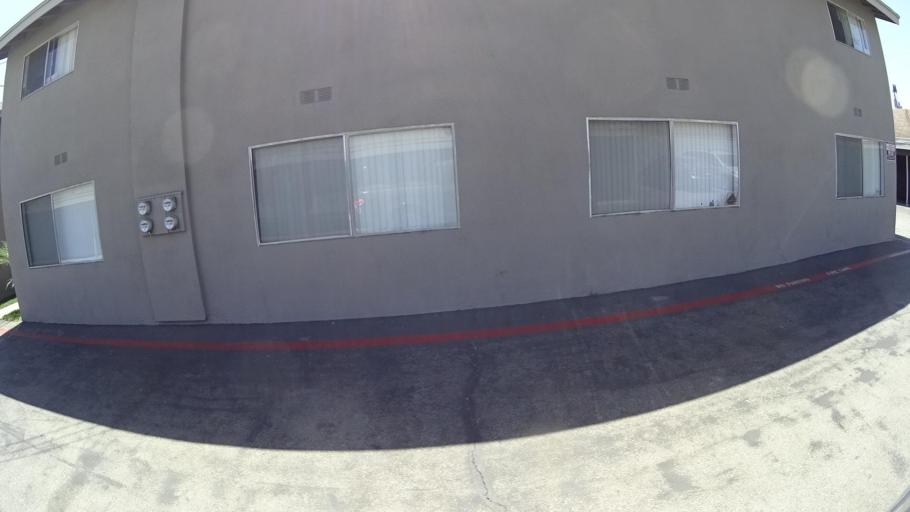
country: US
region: California
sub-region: Orange County
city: Anaheim
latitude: 33.8006
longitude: -117.9084
